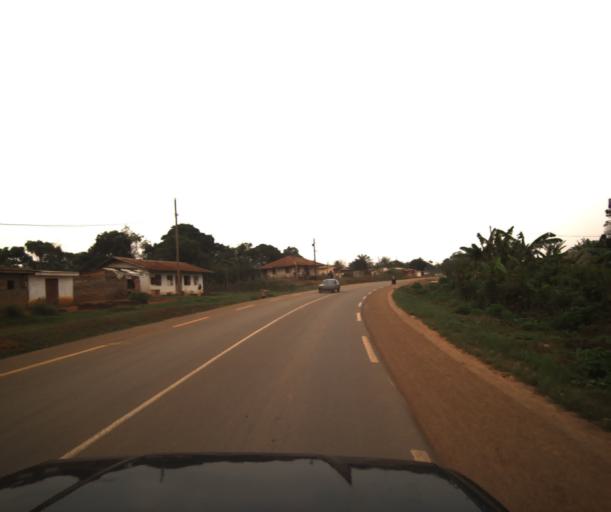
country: CM
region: Centre
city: Mbankomo
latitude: 3.8024
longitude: 11.4614
